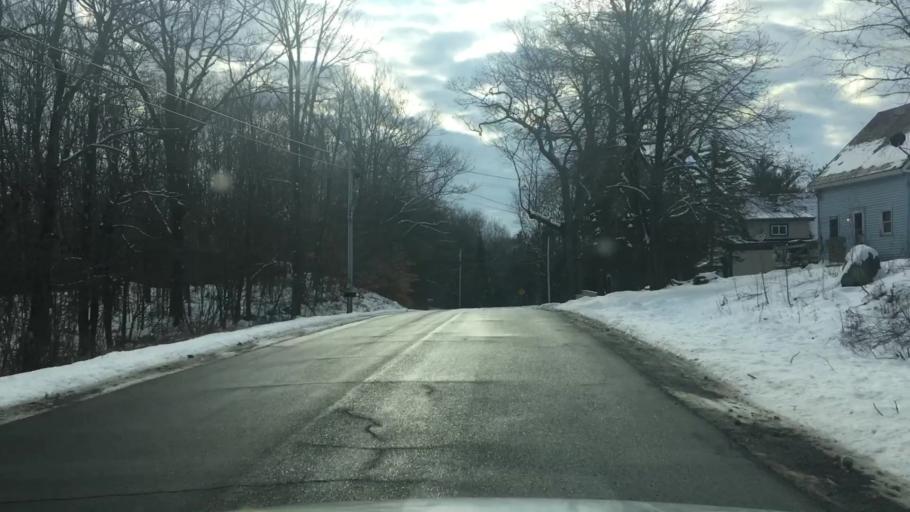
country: US
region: Maine
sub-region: Kennebec County
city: Chelsea
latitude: 44.2861
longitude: -69.6661
